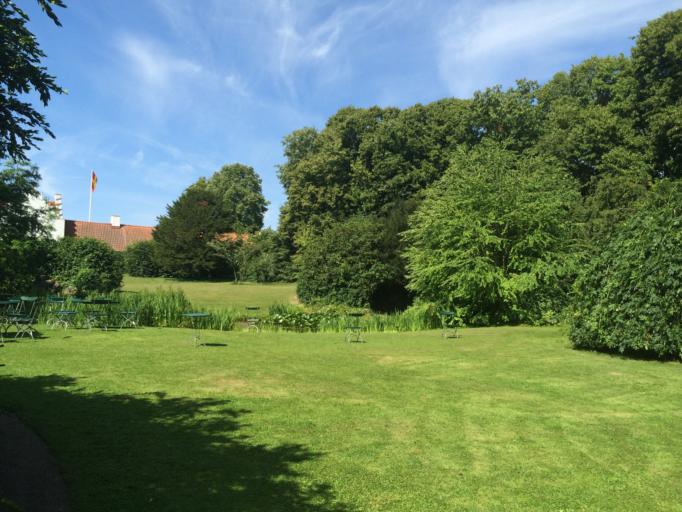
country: SE
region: Skane
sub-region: Vellinge Kommun
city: Vellinge
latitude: 55.4401
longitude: 13.0342
